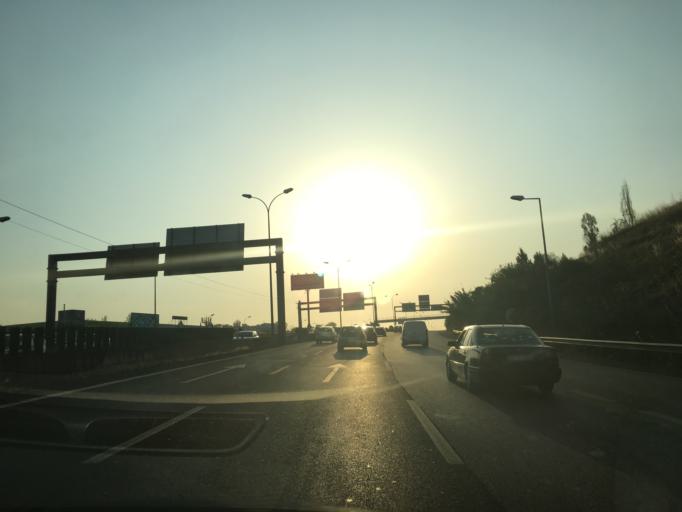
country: PT
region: Lisbon
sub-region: Amadora
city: Amadora
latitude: 38.7423
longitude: -9.2268
